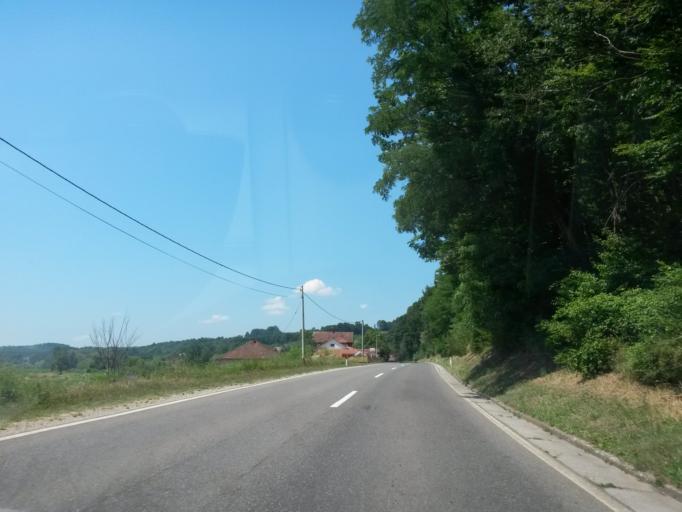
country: BA
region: Federation of Bosnia and Herzegovina
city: Odzak
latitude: 44.9665
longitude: 18.2369
